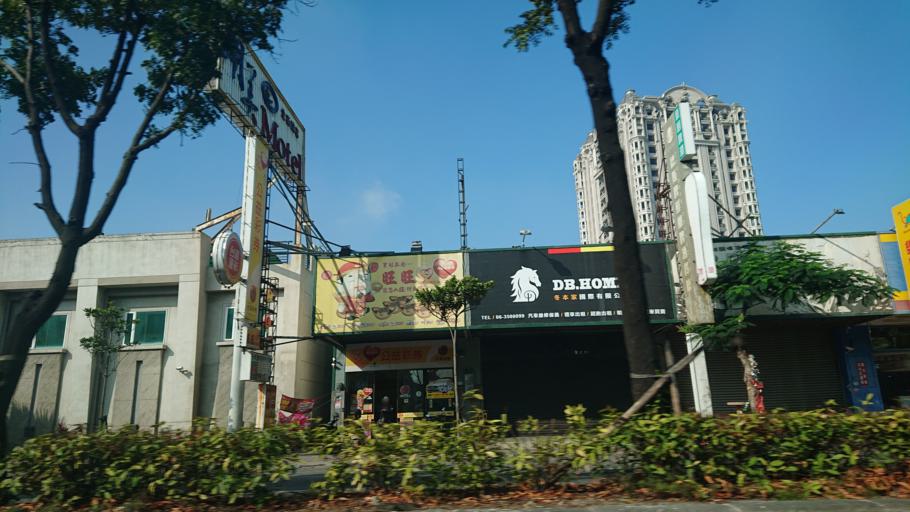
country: TW
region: Taiwan
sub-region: Tainan
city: Tainan
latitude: 23.0055
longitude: 120.1867
